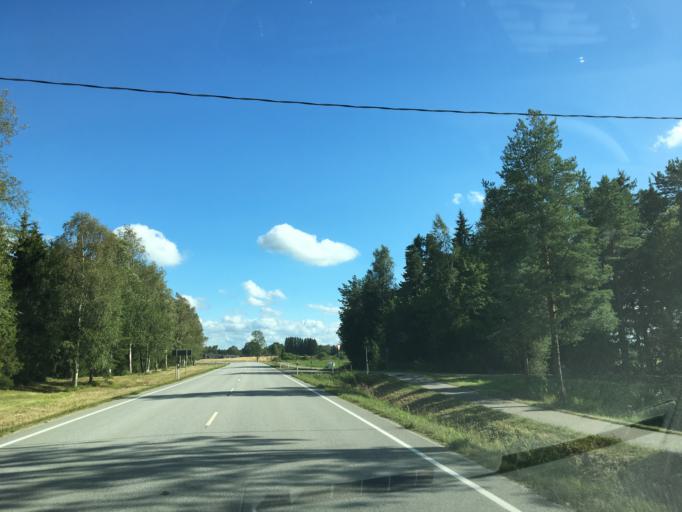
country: EE
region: Paernumaa
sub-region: Vaendra vald (alev)
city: Vandra
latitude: 58.6480
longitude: 25.0692
